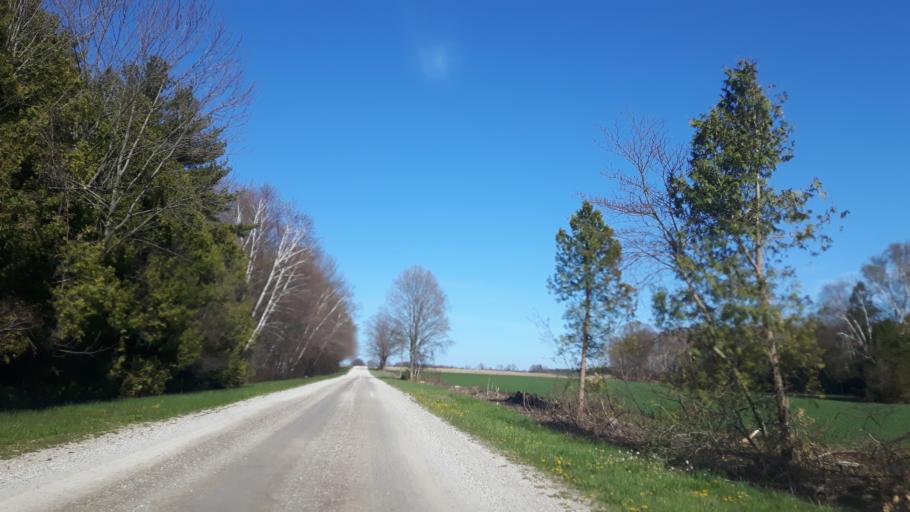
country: CA
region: Ontario
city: Goderich
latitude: 43.6612
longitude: -81.6988
